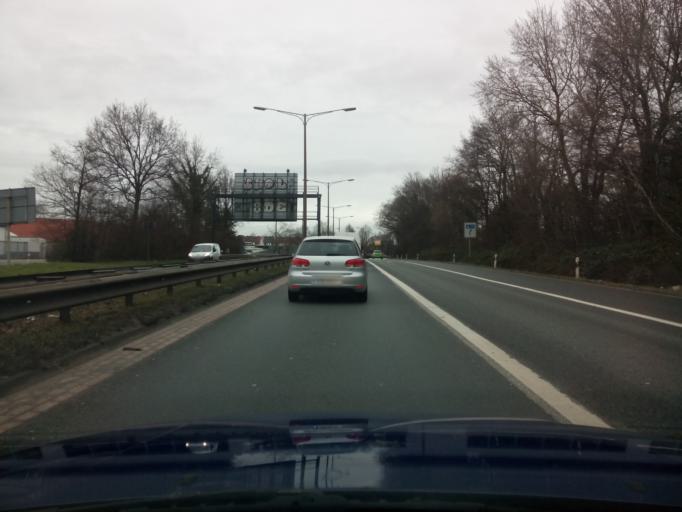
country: DE
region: Bremen
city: Bremen
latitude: 53.0968
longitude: 8.7953
